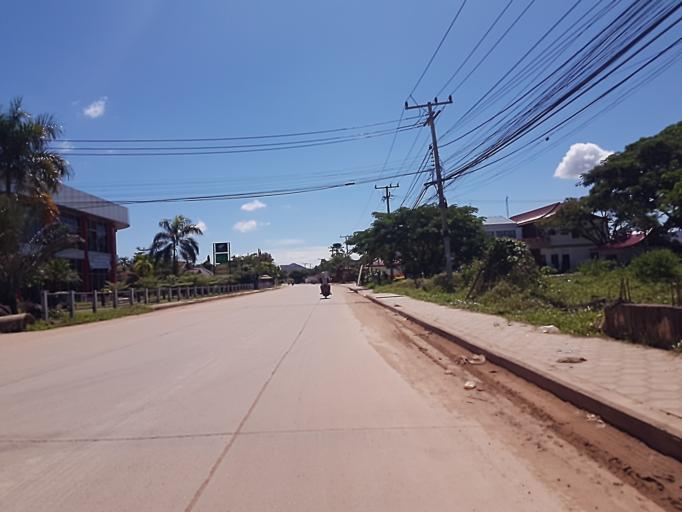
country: LA
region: Vientiane
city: Vientiane
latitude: 17.9403
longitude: 102.6325
